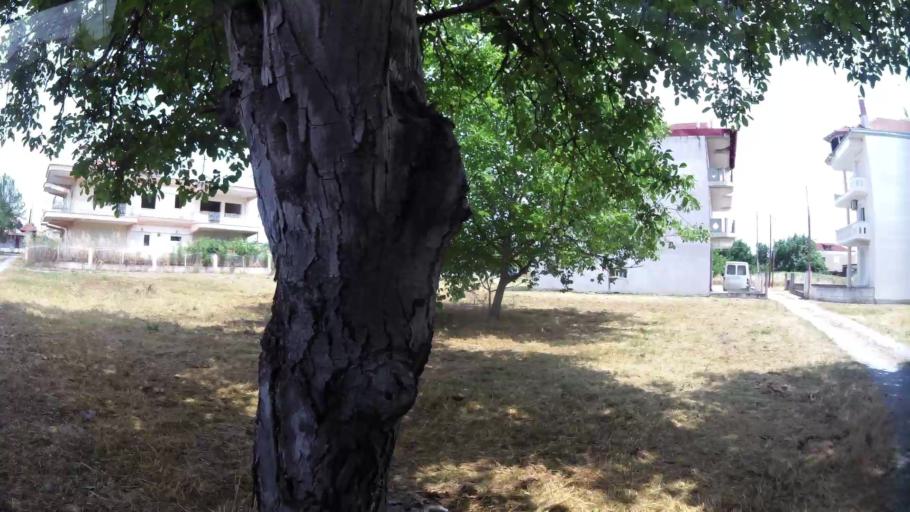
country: GR
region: Central Macedonia
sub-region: Nomos Pierias
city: Peristasi
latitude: 40.2743
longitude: 22.5461
